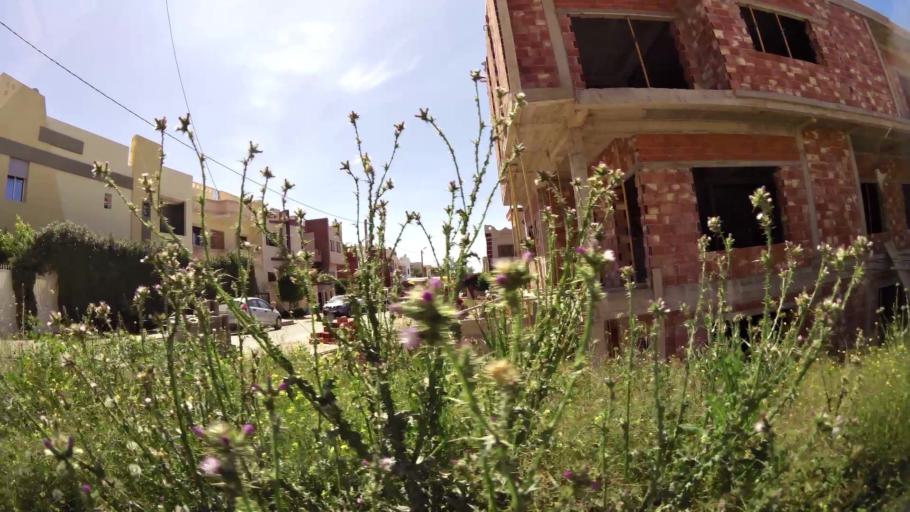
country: MA
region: Oriental
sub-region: Oujda-Angad
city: Oujda
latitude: 34.6471
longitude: -1.9040
